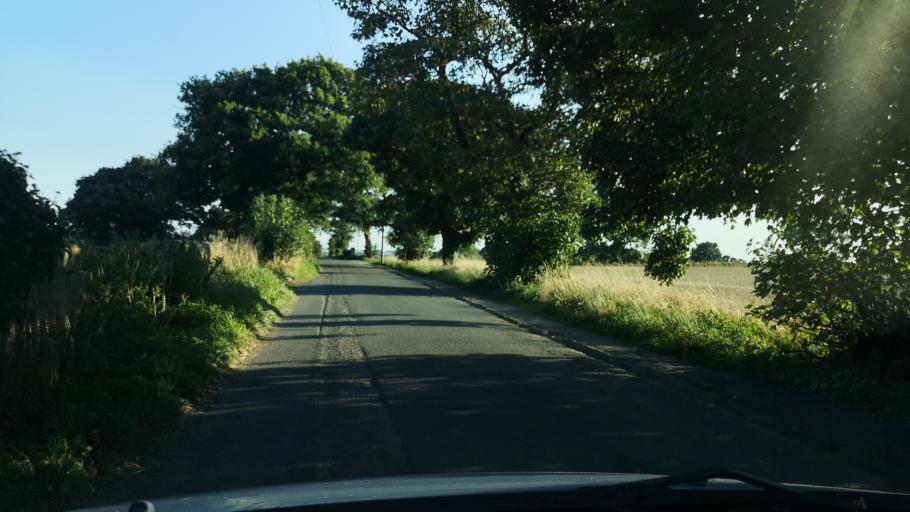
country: GB
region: England
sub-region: City and Borough of Wakefield
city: Low Ackworth
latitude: 53.6565
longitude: -1.3270
